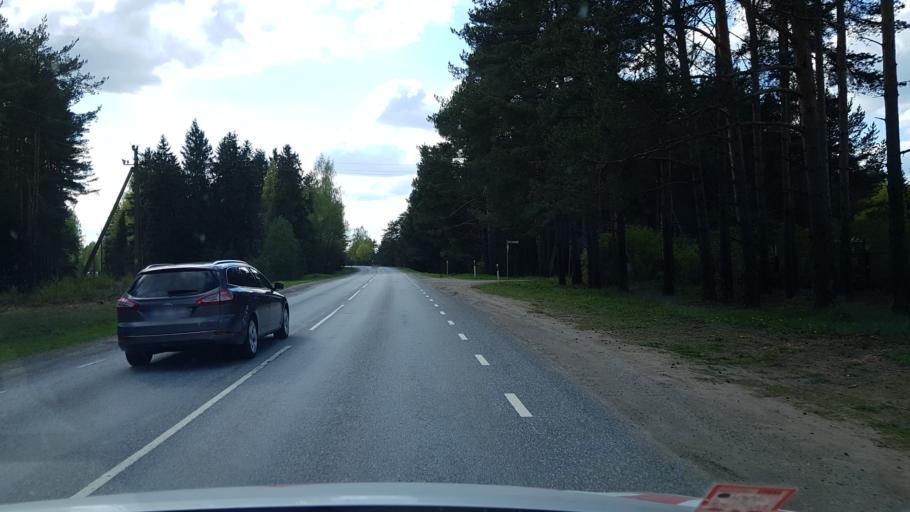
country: EE
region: Tartu
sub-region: UElenurme vald
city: Ulenurme
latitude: 58.3271
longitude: 26.7771
